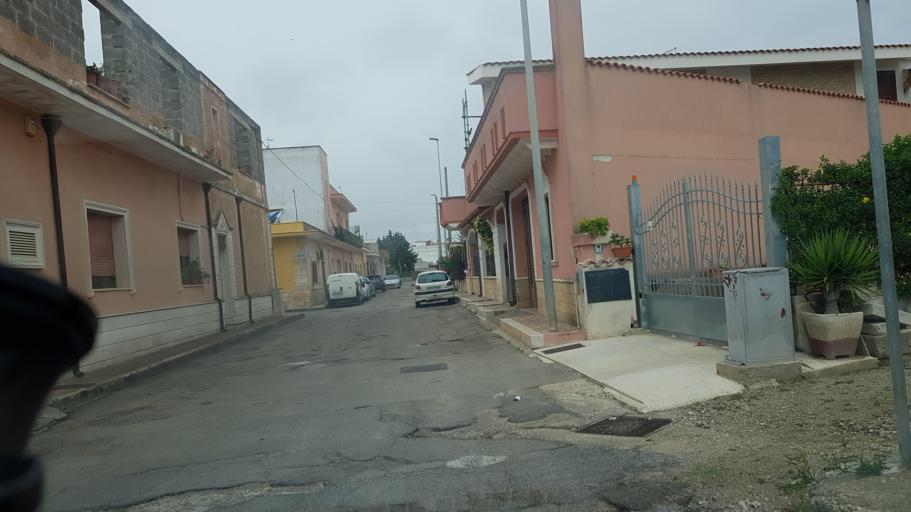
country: IT
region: Apulia
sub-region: Provincia di Brindisi
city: San Pietro Vernotico
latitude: 40.4837
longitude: 18.0055
